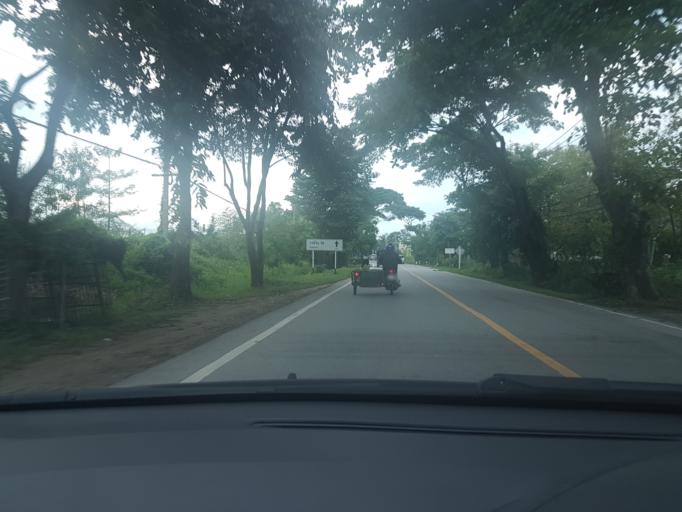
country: TH
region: Chiang Mai
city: San Sai
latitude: 18.8766
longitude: 99.0434
